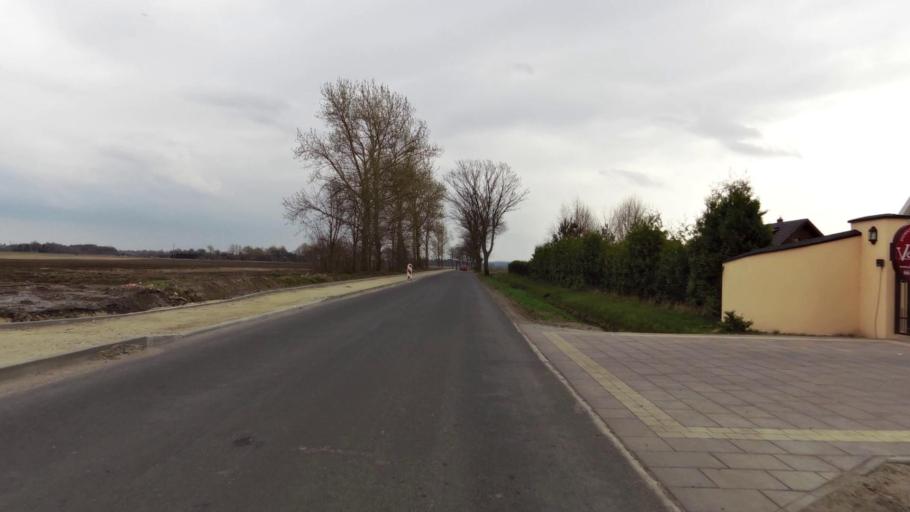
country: PL
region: West Pomeranian Voivodeship
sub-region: Powiat koszalinski
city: Sianow
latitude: 54.2789
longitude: 16.2209
